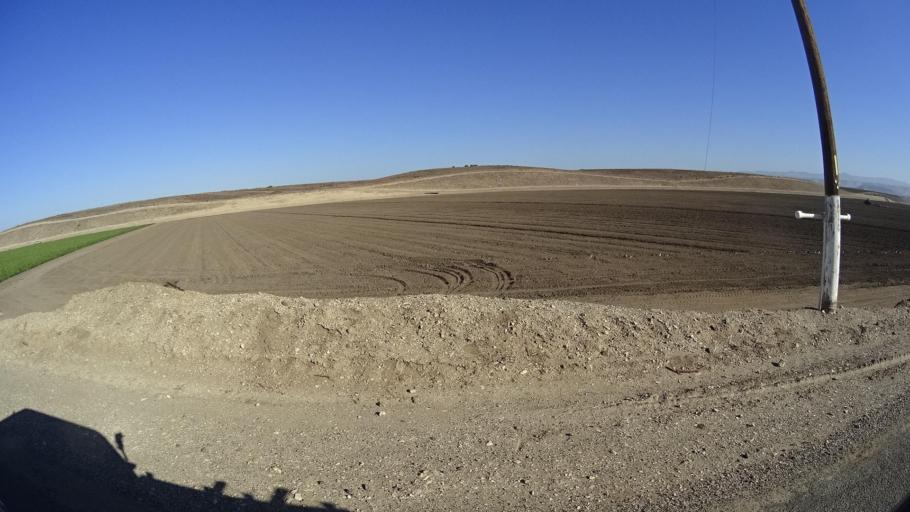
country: US
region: California
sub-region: Monterey County
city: King City
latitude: 36.1074
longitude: -121.0467
